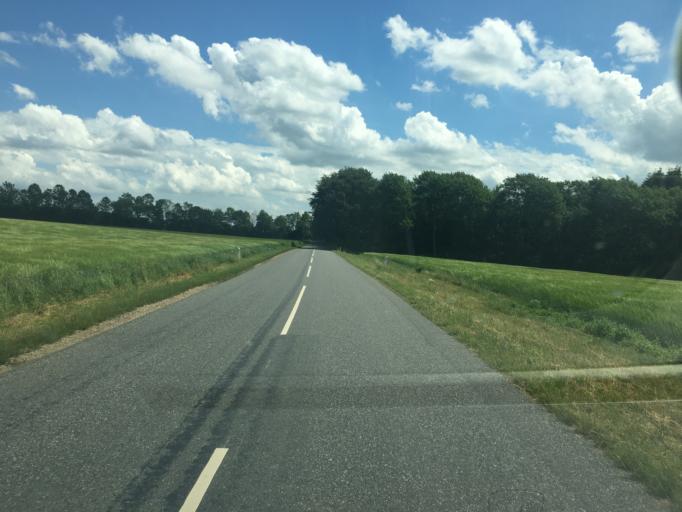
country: DK
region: South Denmark
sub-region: Haderslev Kommune
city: Vojens
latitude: 55.2800
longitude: 9.3198
